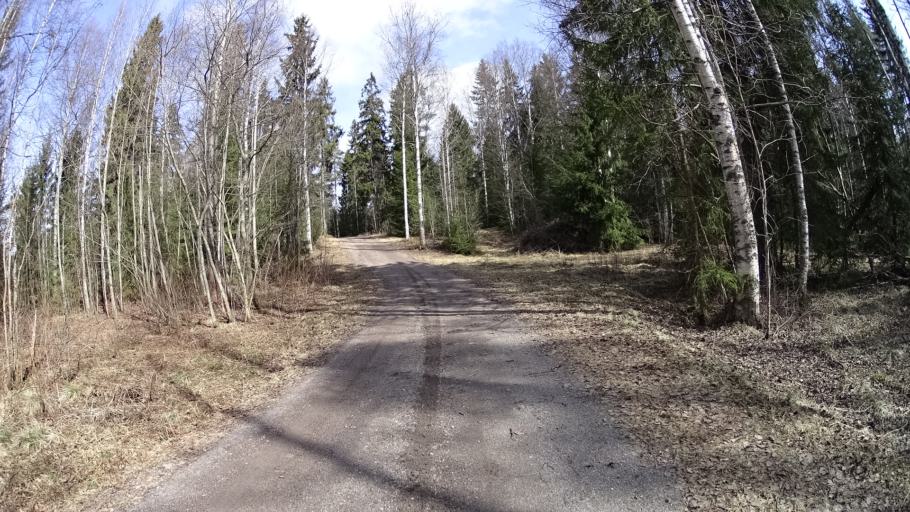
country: FI
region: Uusimaa
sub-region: Helsinki
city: Kilo
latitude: 60.3166
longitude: 24.8126
